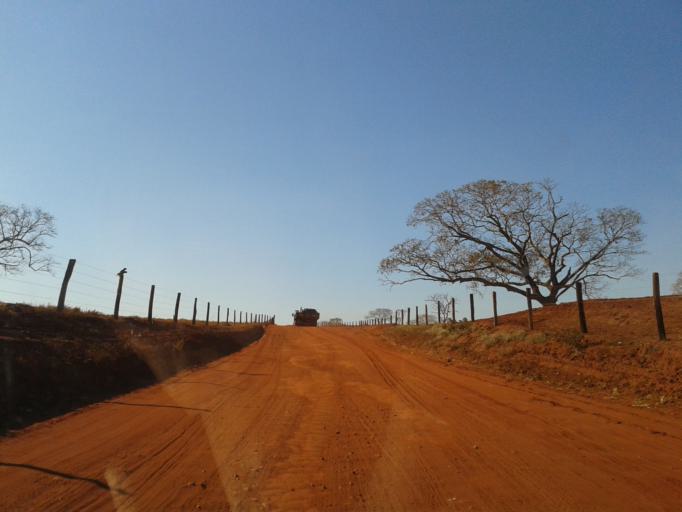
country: BR
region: Minas Gerais
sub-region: Ituiutaba
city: Ituiutaba
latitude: -18.9777
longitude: -49.4100
